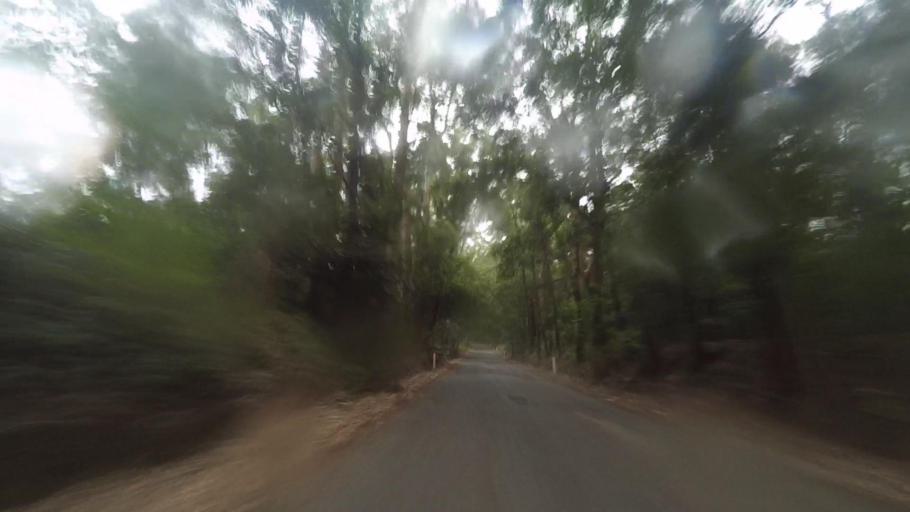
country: AU
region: New South Wales
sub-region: Wollongong
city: Mount Keira
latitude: -34.4046
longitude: 150.8215
